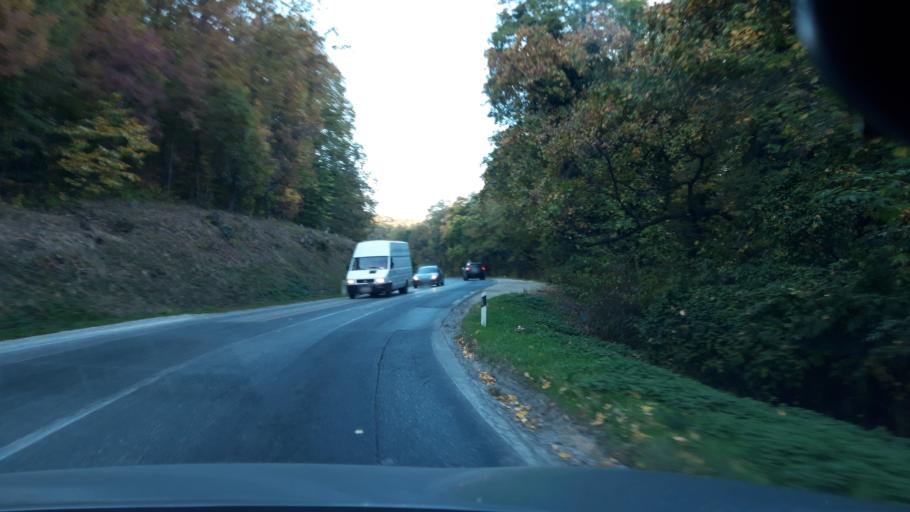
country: RS
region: Autonomna Pokrajina Vojvodina
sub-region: Sremski Okrug
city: Irig
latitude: 45.1391
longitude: 19.8374
